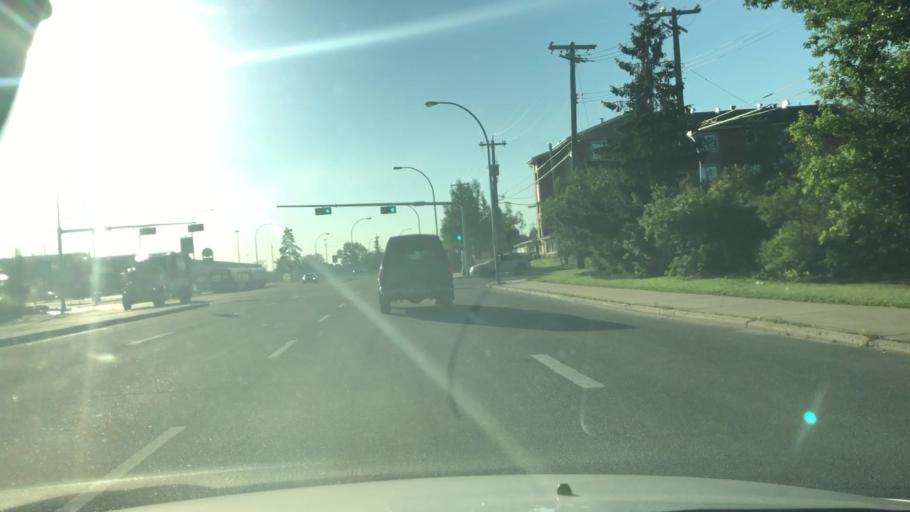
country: CA
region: Alberta
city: Edmonton
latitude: 53.5383
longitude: -113.4246
